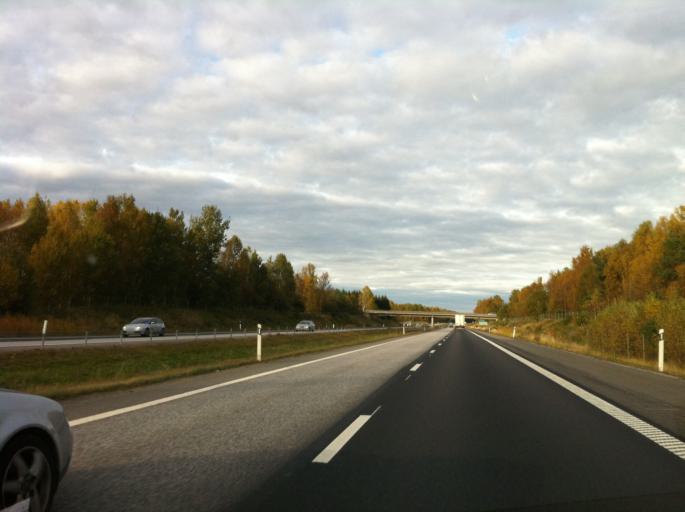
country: SE
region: OErebro
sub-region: Hallsbergs Kommun
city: Hallsberg
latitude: 59.0949
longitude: 15.0512
